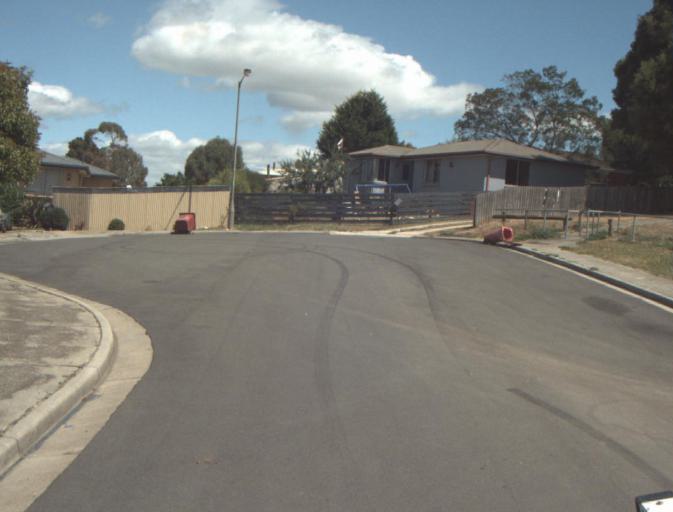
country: AU
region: Tasmania
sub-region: Launceston
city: Newstead
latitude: -41.4088
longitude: 147.1686
